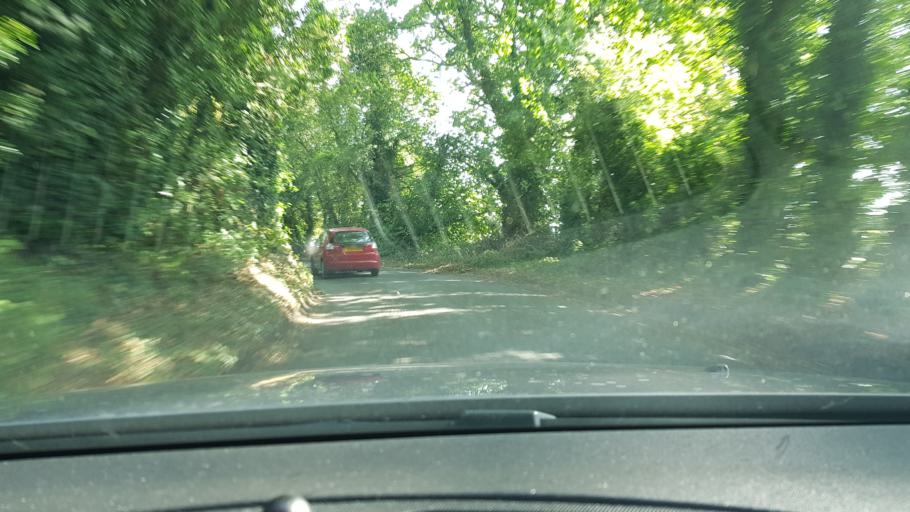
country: GB
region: England
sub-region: Wiltshire
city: Ramsbury
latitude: 51.4504
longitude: -1.5937
